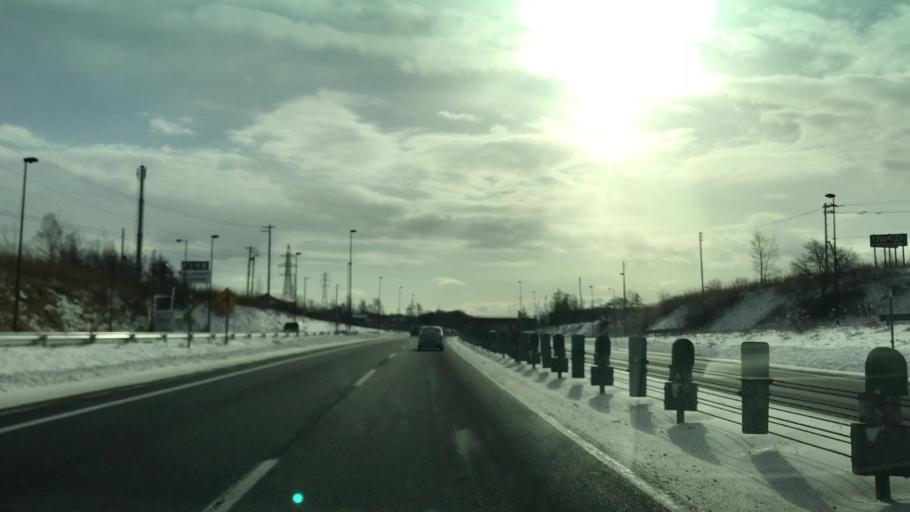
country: JP
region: Hokkaido
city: Kitahiroshima
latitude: 42.9507
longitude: 141.5130
